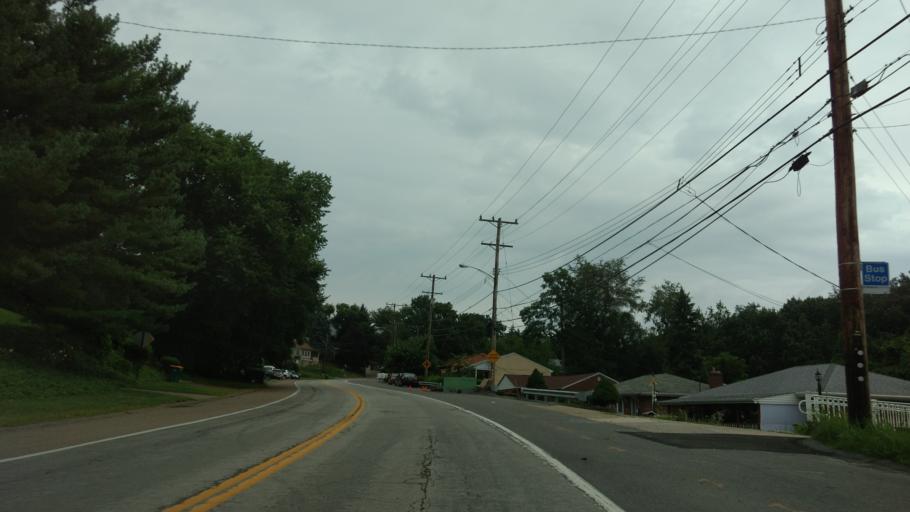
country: US
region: Pennsylvania
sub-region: Allegheny County
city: West View
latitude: 40.5118
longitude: -80.0452
